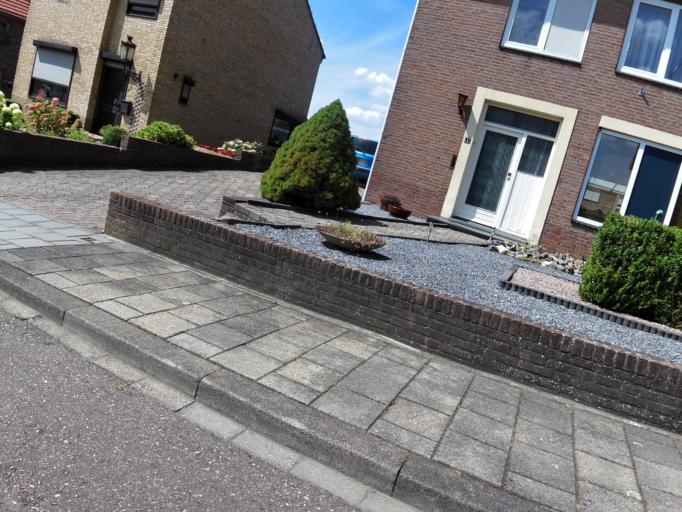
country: NL
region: Limburg
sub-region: Valkenburg aan de Geul
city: Schin op Geul
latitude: 50.8355
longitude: 5.8943
